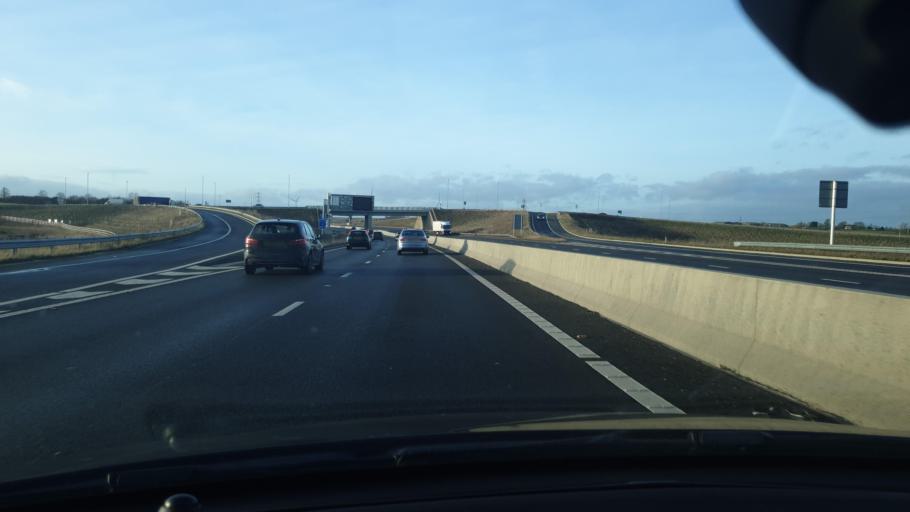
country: GB
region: England
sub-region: Cambridgeshire
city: Brampton
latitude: 52.3305
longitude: -0.2540
